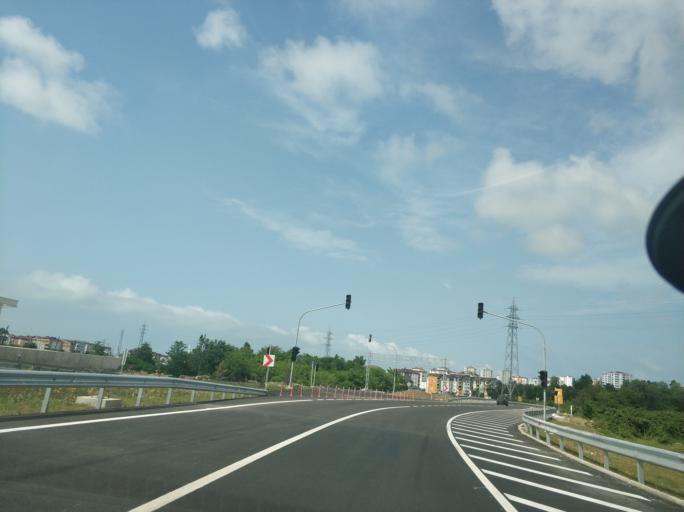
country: TR
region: Ordu
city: Ordu
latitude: 40.9584
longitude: 37.9046
